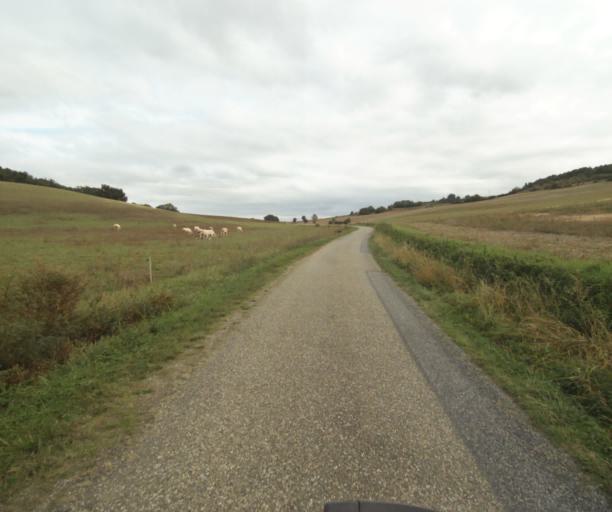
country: FR
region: Midi-Pyrenees
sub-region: Departement du Tarn-et-Garonne
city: Beaumont-de-Lomagne
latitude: 43.8283
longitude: 1.0713
